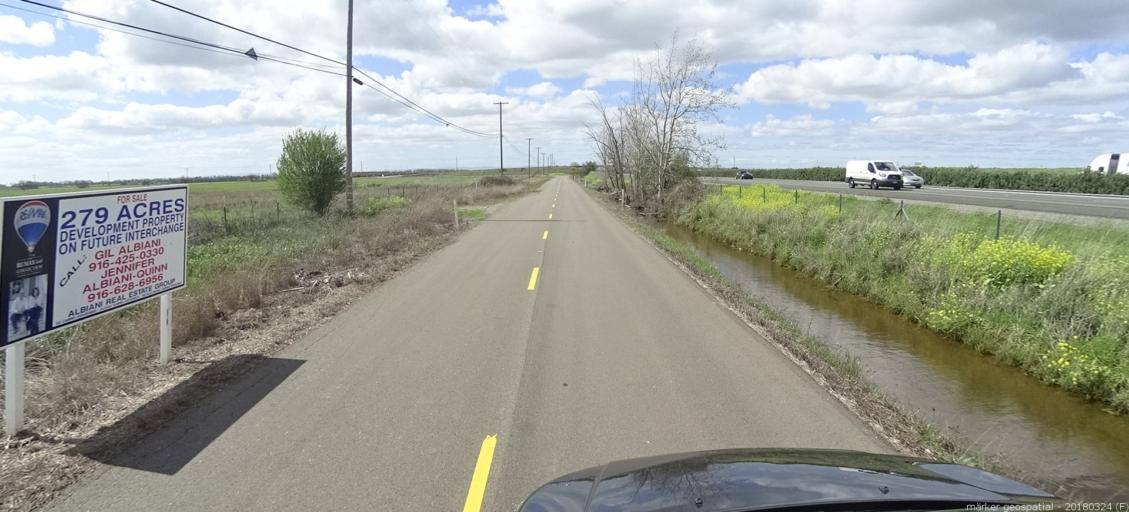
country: US
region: California
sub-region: Yolo County
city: West Sacramento
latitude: 38.6708
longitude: -121.5709
